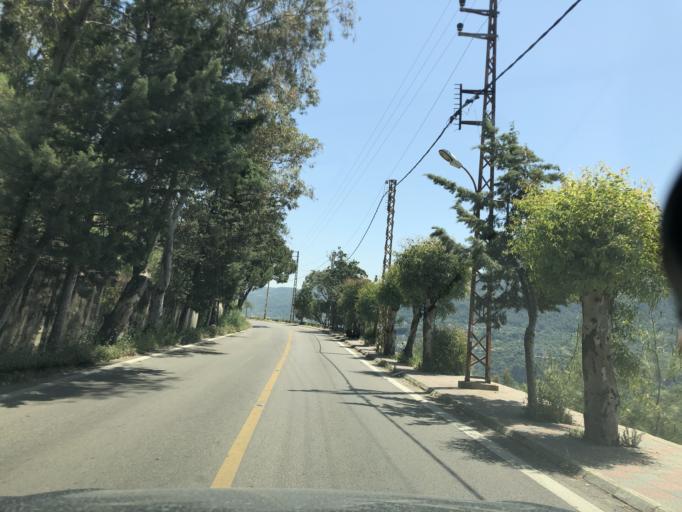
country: LB
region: Mont-Liban
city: Beit ed Dine
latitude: 33.6875
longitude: 35.5237
